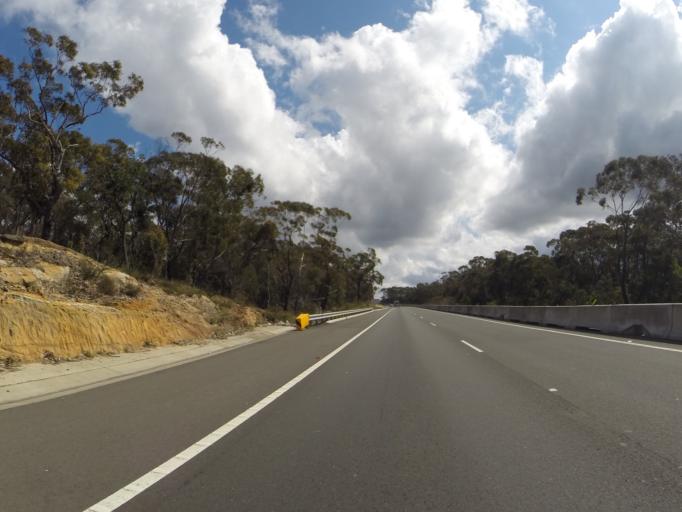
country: AU
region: New South Wales
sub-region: Wollongong
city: Mount Keira
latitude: -34.3644
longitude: 150.8235
